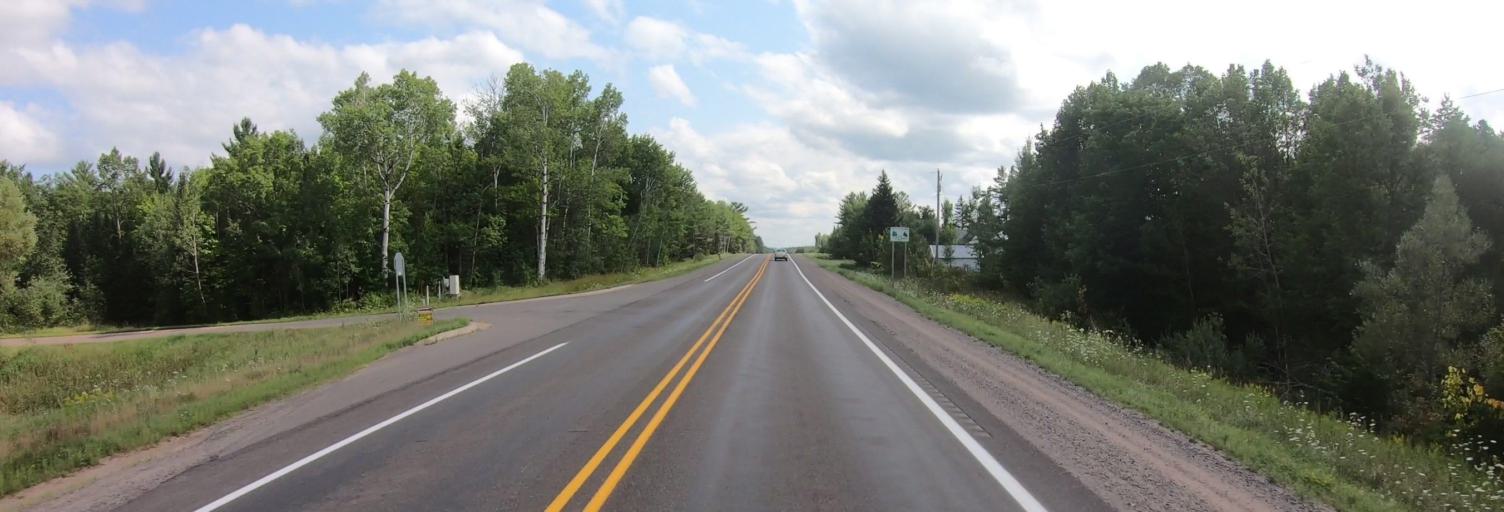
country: US
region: Michigan
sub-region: Ontonagon County
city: Ontonagon
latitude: 46.5788
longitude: -89.1785
